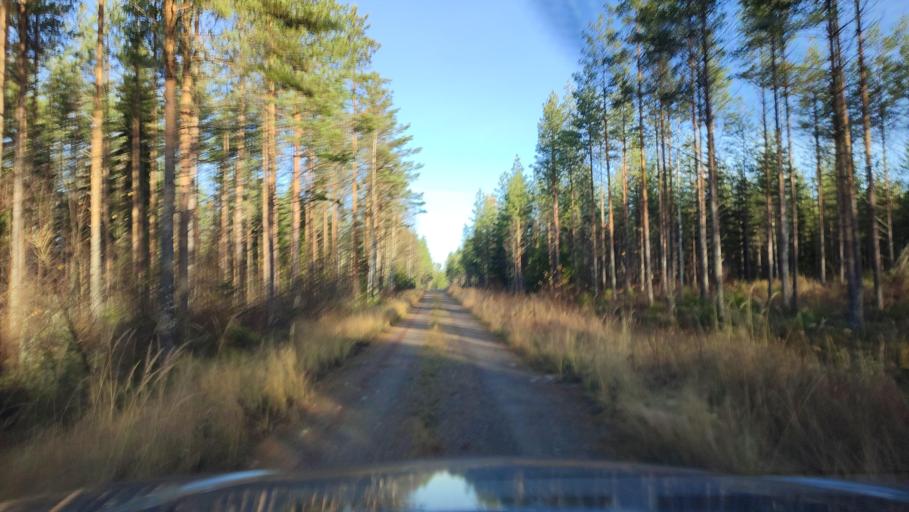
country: FI
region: Southern Ostrobothnia
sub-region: Suupohja
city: Karijoki
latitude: 62.1904
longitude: 21.6070
